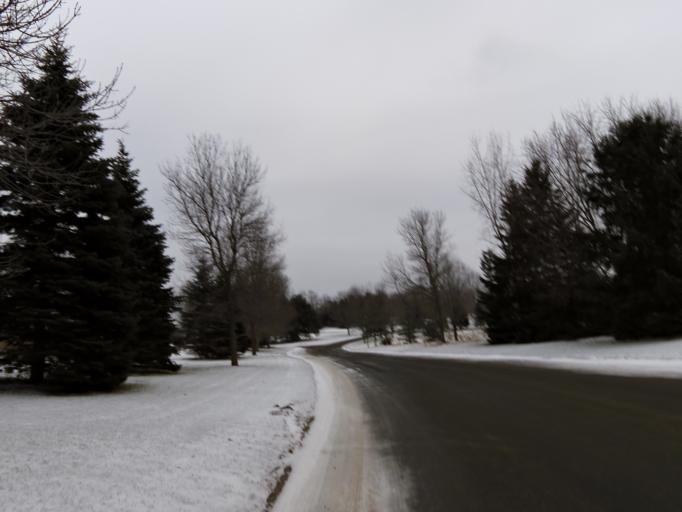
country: US
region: Minnesota
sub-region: Washington County
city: Lake Elmo
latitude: 44.9630
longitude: -92.8302
